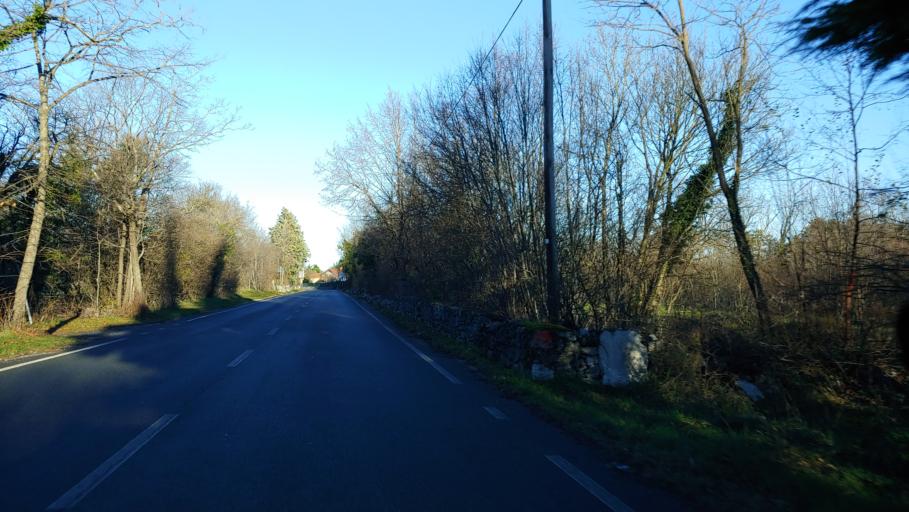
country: IT
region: Friuli Venezia Giulia
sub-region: Provincia di Trieste
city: Villa Opicina
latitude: 45.6678
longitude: 13.8300
